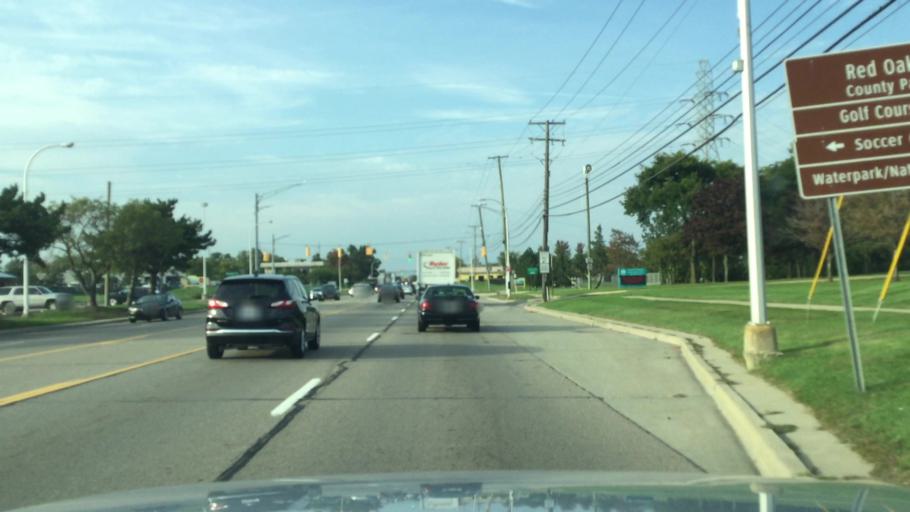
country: US
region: Michigan
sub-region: Oakland County
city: Madison Heights
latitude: 42.5078
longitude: -83.1058
